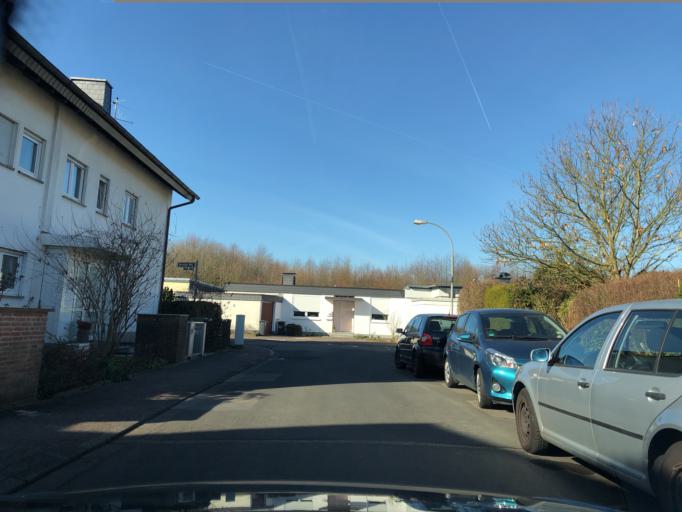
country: DE
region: Hesse
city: Kelsterbach
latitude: 50.0835
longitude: 8.5681
